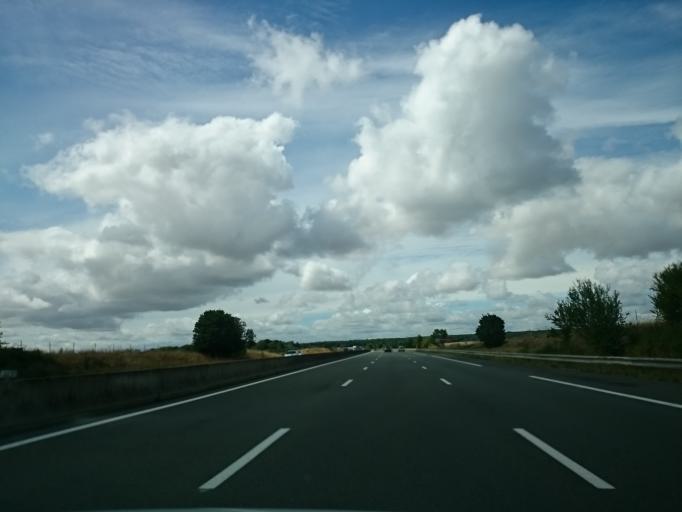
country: FR
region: Centre
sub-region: Departement d'Eure-et-Loir
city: Brou
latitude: 48.2771
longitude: 1.1864
